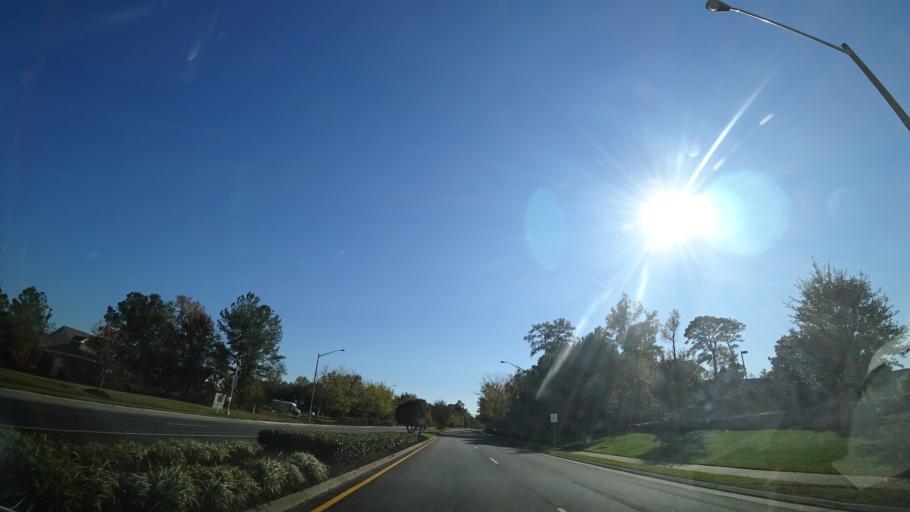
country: US
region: Virginia
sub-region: City of Portsmouth
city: Portsmouth Heights
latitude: 36.8849
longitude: -76.4372
